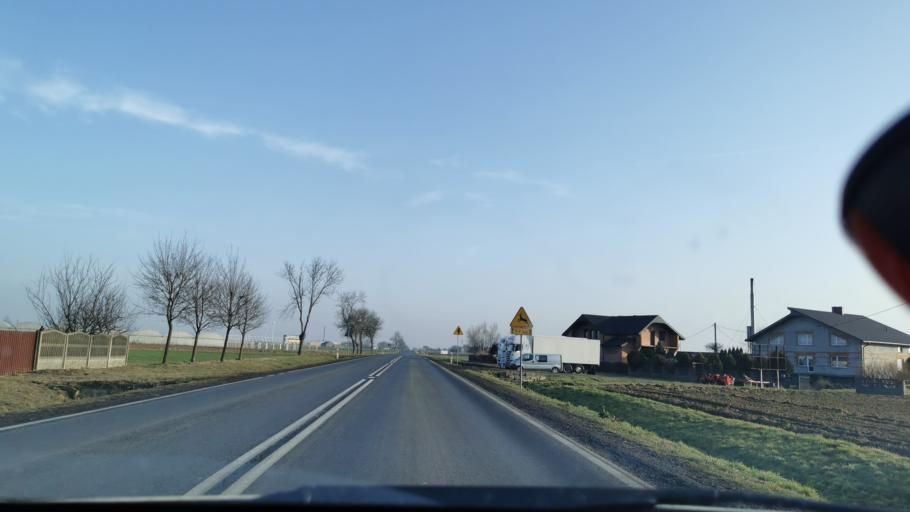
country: PL
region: Lodz Voivodeship
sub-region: Powiat sieradzki
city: Blaszki
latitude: 51.6841
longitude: 18.3326
